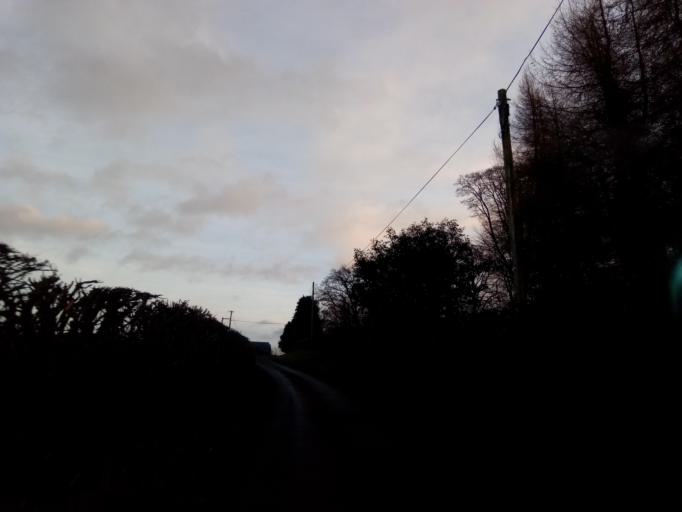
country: GB
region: Scotland
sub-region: The Scottish Borders
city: Newtown St Boswells
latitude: 55.5353
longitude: -2.7122
